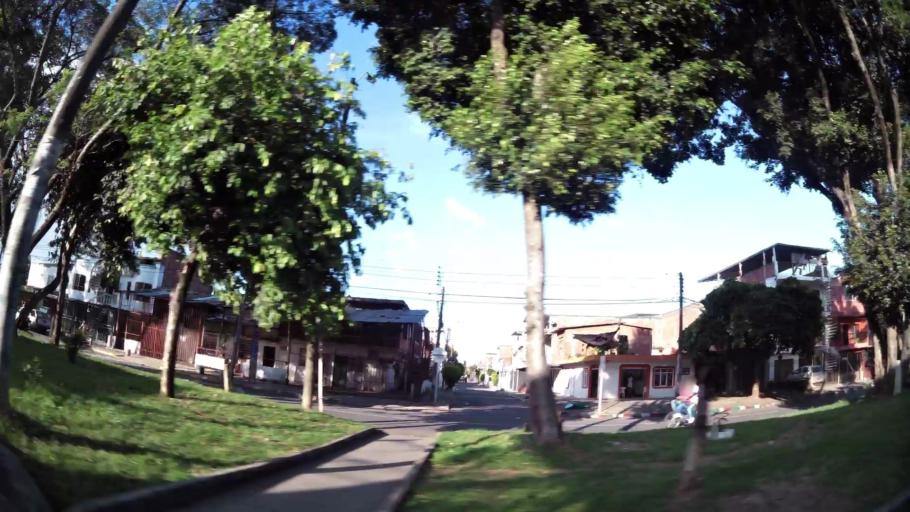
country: CO
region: Valle del Cauca
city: Cali
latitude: 3.4119
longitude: -76.5076
